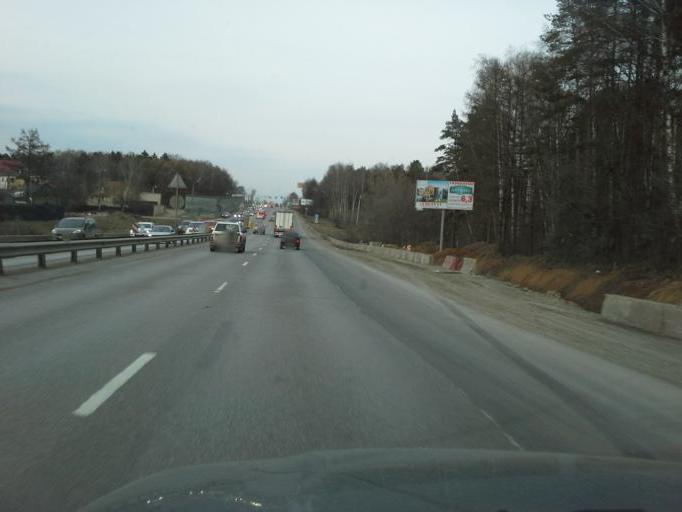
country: RU
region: Moskovskaya
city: Odintsovo
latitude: 55.6649
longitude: 37.3063
